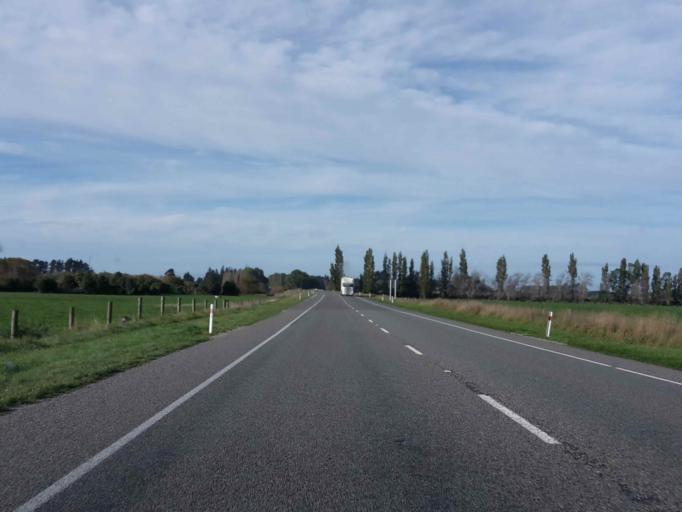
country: NZ
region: Canterbury
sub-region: Timaru District
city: Pleasant Point
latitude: -44.0550
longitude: 171.3971
